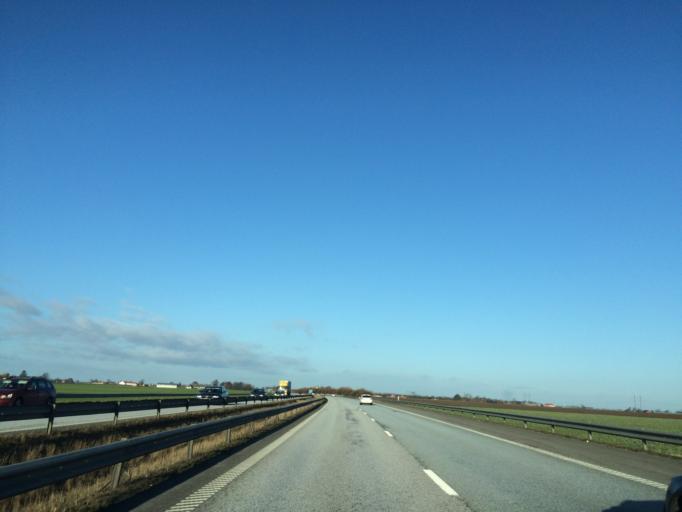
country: SE
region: Skane
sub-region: Lomma Kommun
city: Lomma
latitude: 55.7017
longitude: 13.0977
